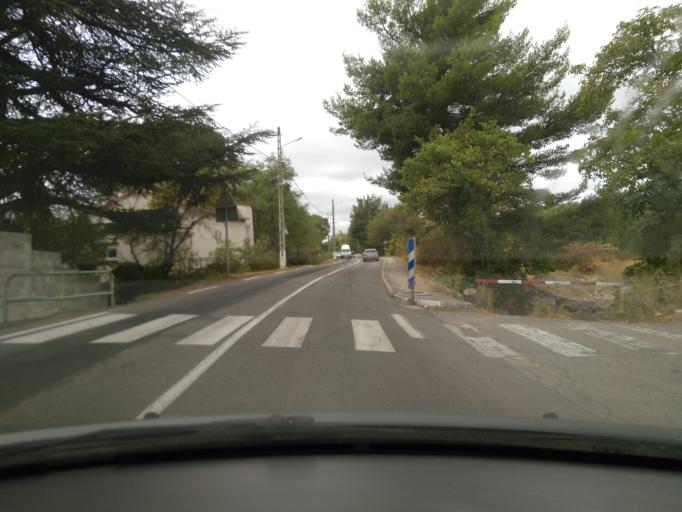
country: FR
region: Rhone-Alpes
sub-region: Departement de la Drome
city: Nyons
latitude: 44.3557
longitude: 5.1242
